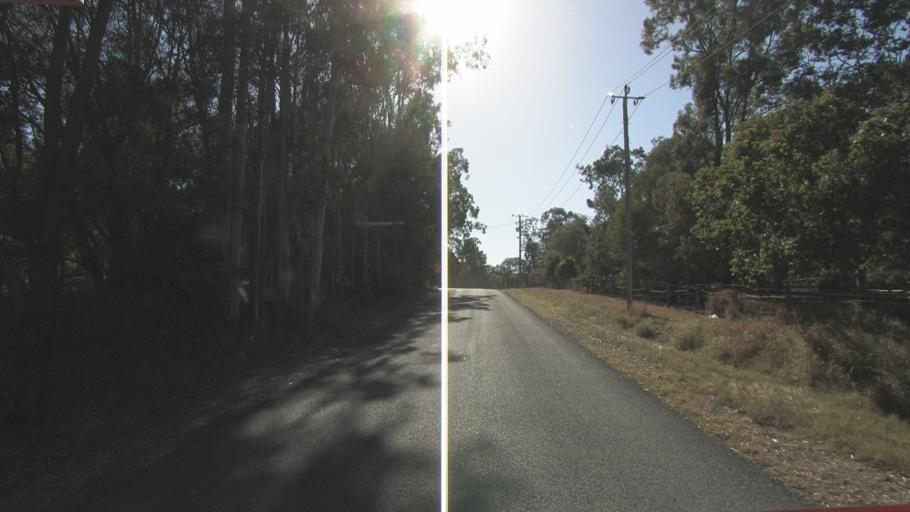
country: AU
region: Queensland
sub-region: Logan
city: Cedar Vale
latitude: -27.8386
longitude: 152.9961
